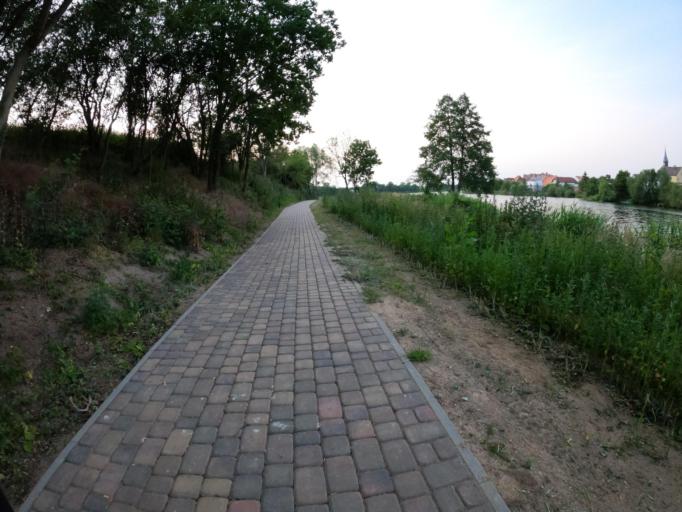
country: PL
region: West Pomeranian Voivodeship
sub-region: Powiat choszczenski
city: Pelczyce
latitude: 53.0397
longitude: 15.2968
